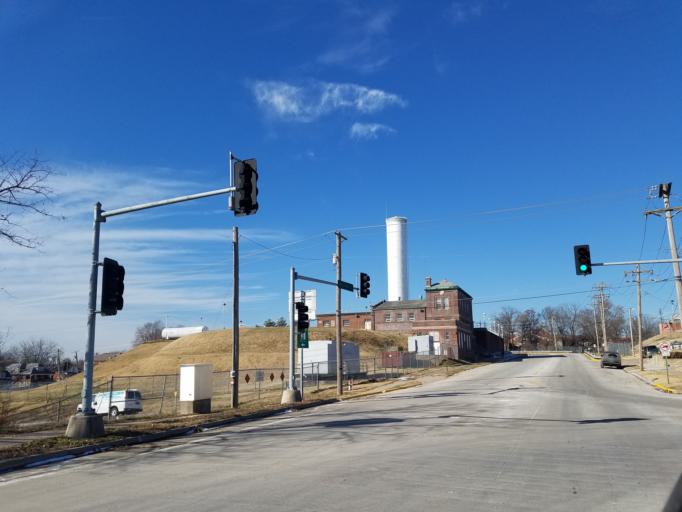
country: US
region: Missouri
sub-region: Cole County
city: Jefferson City
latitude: 38.5798
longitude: -92.1727
